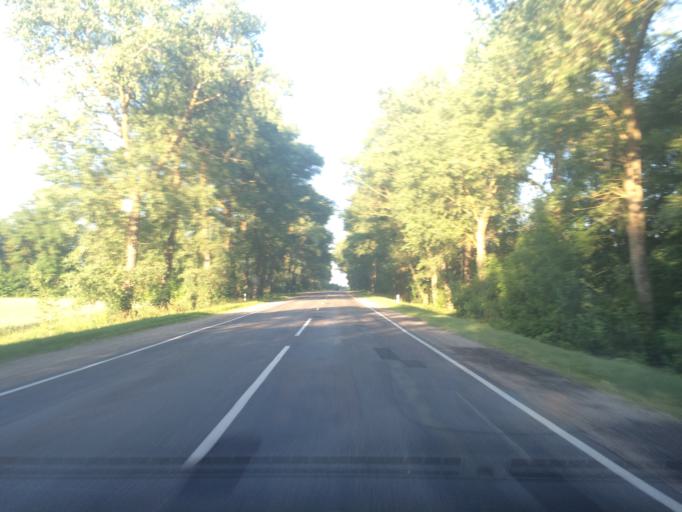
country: LT
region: Utenos apskritis
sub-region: Anyksciai
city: Anyksciai
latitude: 55.3701
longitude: 25.0121
